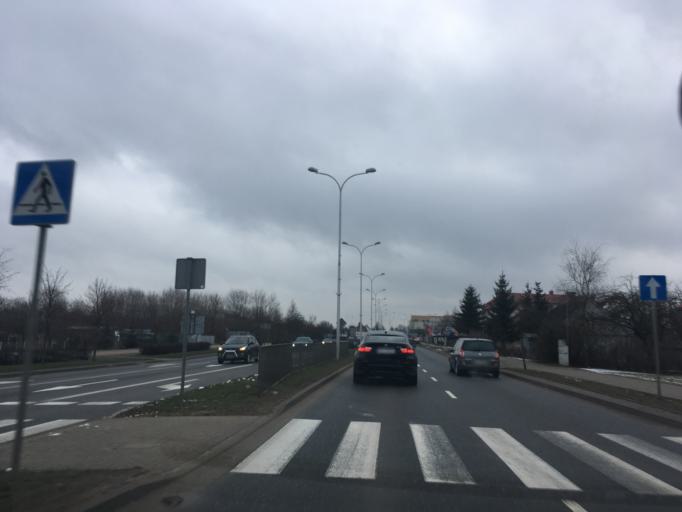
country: PL
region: Podlasie
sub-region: Suwalki
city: Suwalki
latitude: 54.1139
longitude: 22.9284
